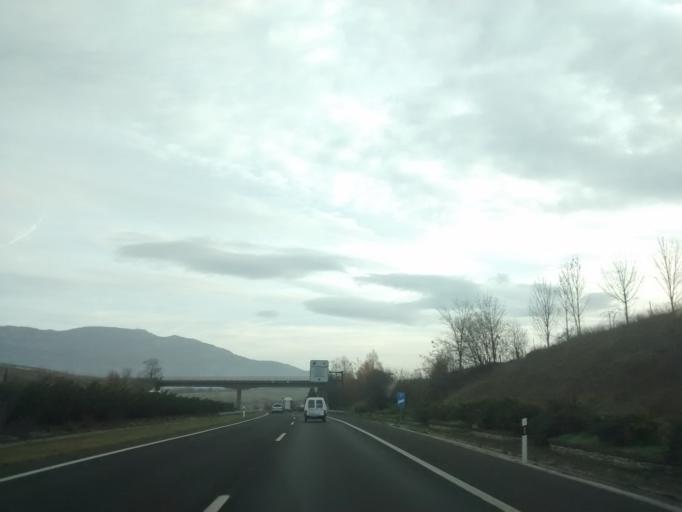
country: ES
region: Navarre
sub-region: Provincia de Navarra
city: Arbizu
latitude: 42.9069
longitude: -2.0444
